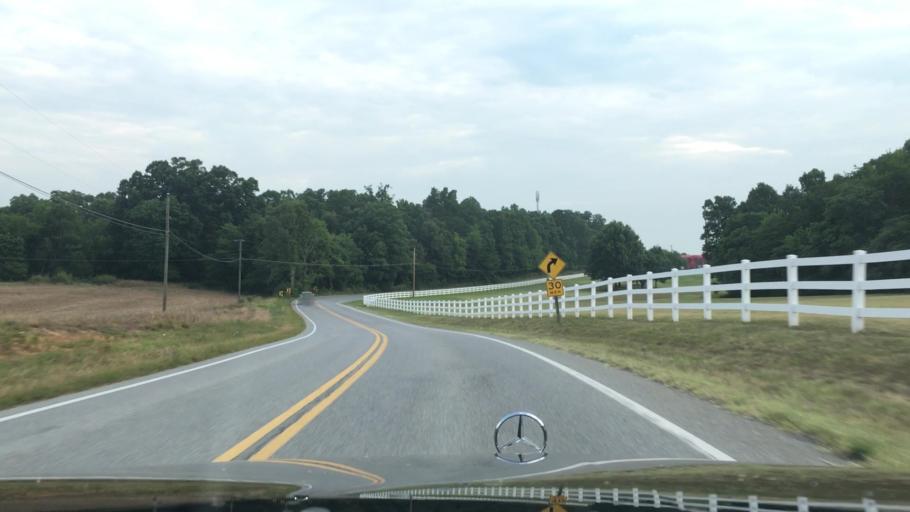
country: US
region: Virginia
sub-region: Campbell County
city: Timberlake
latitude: 37.3012
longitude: -79.3100
